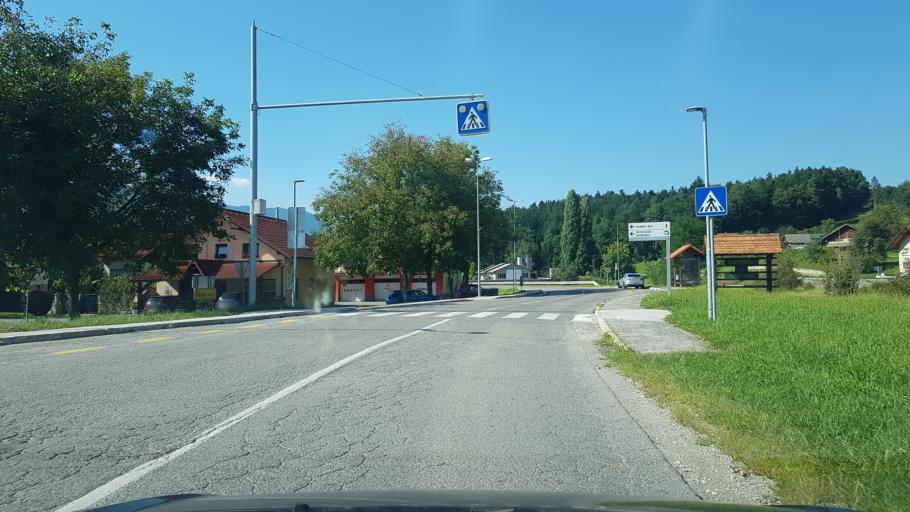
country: SI
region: Smartno ob Paki
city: Smartno ob Paki
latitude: 46.3414
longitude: 15.0191
